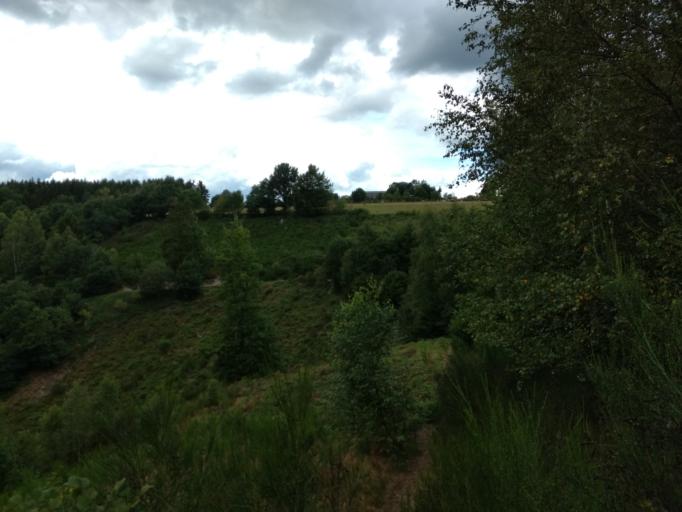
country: BE
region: Wallonia
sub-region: Province du Luxembourg
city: Houffalize
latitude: 50.1472
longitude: 5.7341
